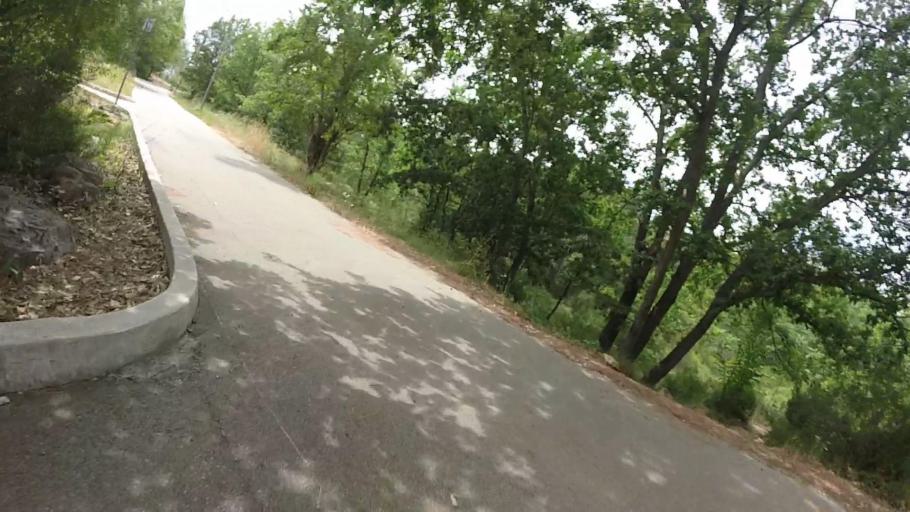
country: FR
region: Provence-Alpes-Cote d'Azur
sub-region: Departement des Alpes-Maritimes
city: Biot
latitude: 43.6239
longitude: 7.0548
